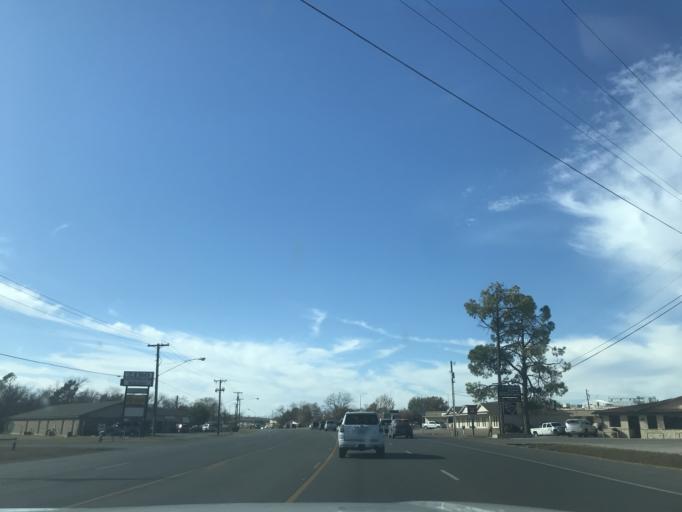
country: US
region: Texas
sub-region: Erath County
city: Stephenville
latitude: 32.2071
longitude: -98.2235
